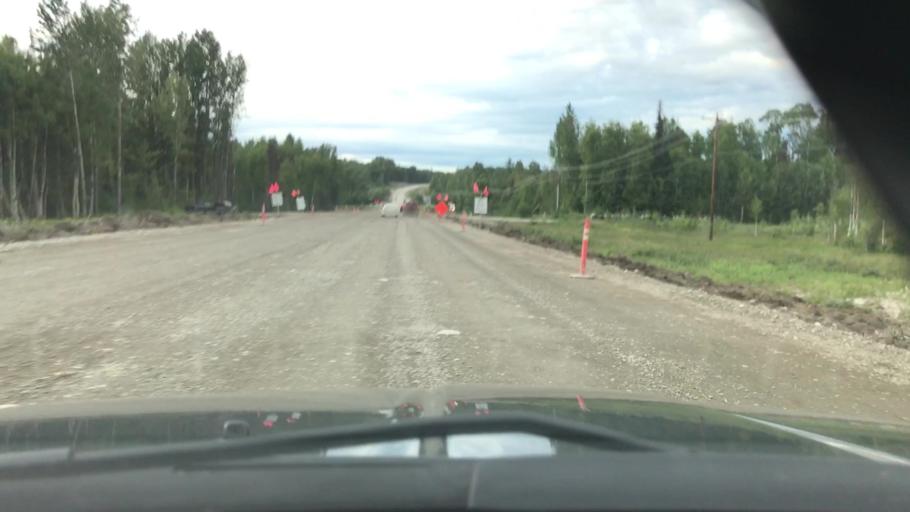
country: US
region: Alaska
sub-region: Matanuska-Susitna Borough
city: Y
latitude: 62.0992
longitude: -150.0611
